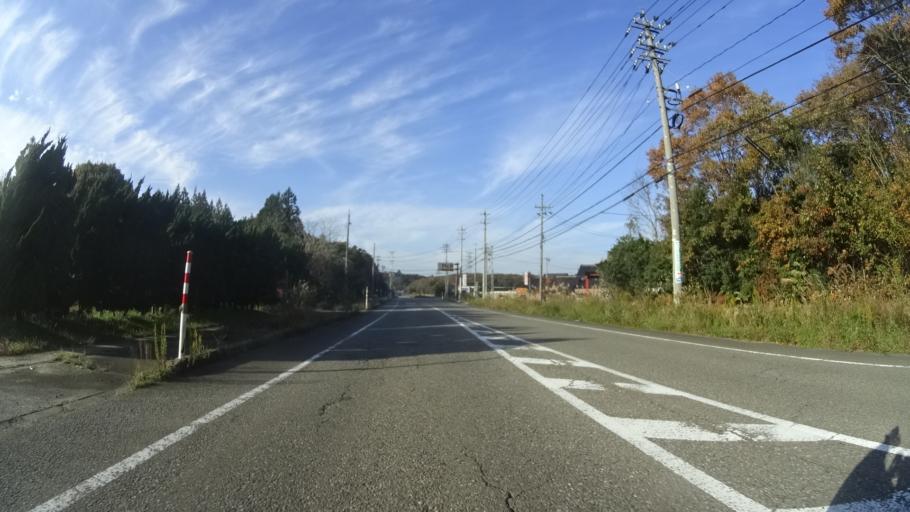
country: JP
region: Ishikawa
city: Hakui
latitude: 37.0399
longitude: 136.7781
